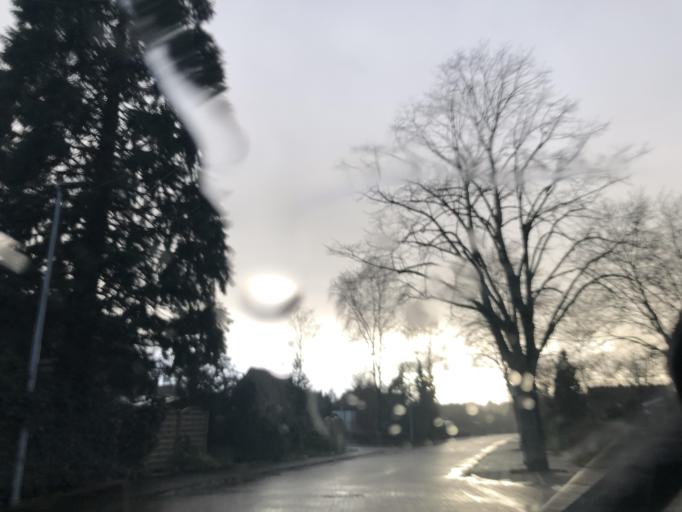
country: DE
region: Lower Saxony
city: Bad Fallingbostel
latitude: 52.8750
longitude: 9.7012
